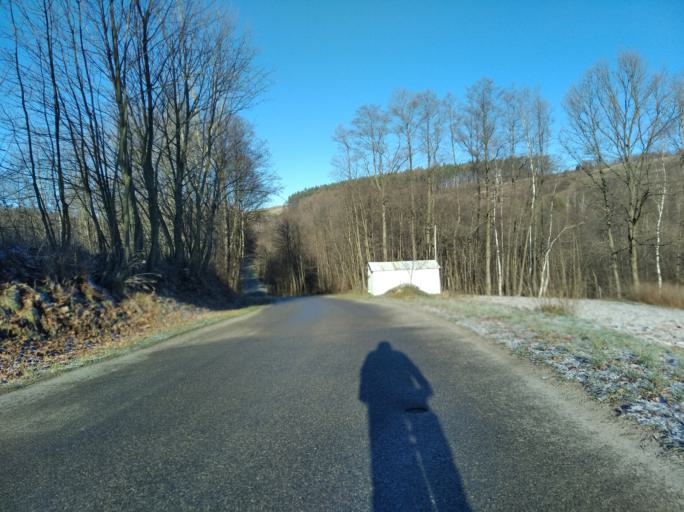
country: PL
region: Subcarpathian Voivodeship
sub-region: Powiat strzyzowski
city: Czudec
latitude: 49.9433
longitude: 21.7873
